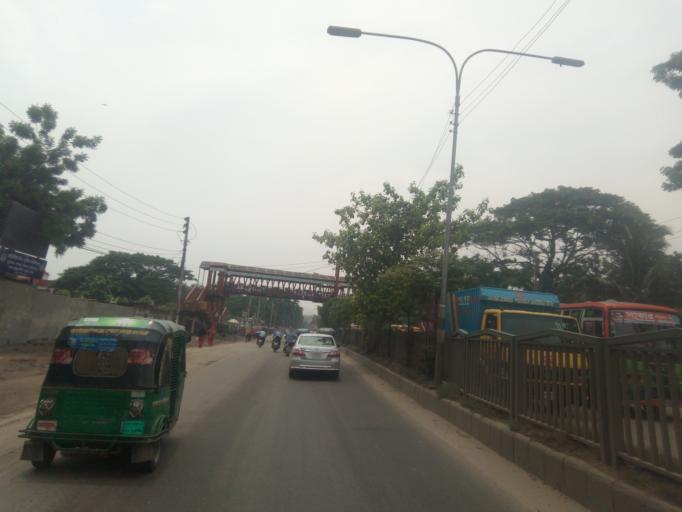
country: BD
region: Dhaka
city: Azimpur
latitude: 23.7801
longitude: 90.3546
